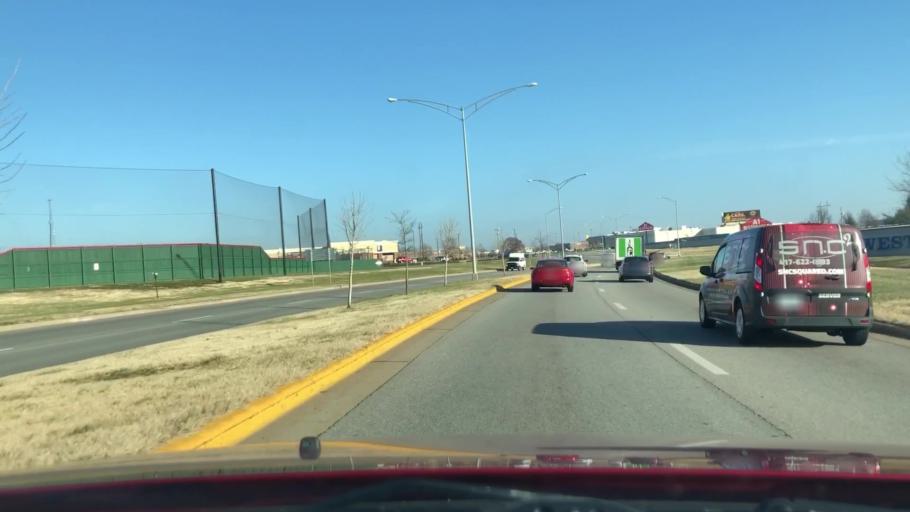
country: US
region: Missouri
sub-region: Greene County
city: Springfield
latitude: 37.1549
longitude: -93.3185
